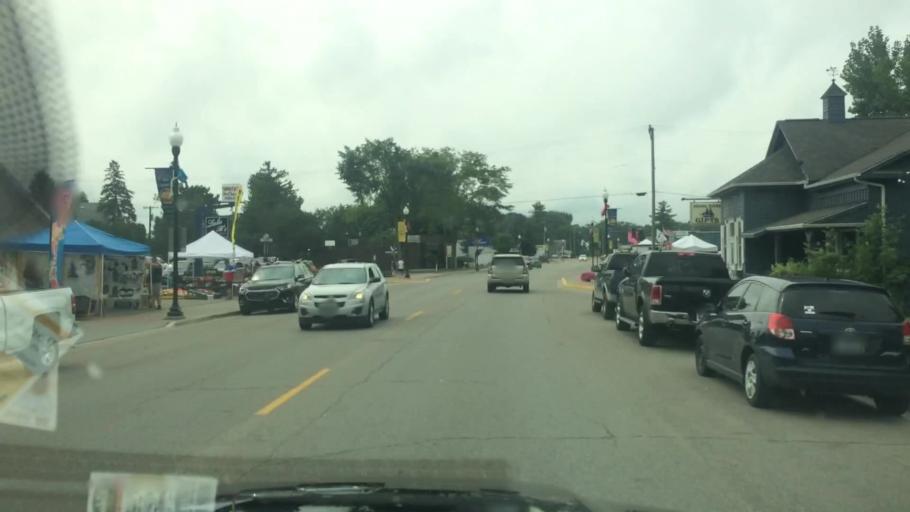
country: US
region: Michigan
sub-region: Huron County
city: Pigeon
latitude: 43.9409
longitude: -83.2725
